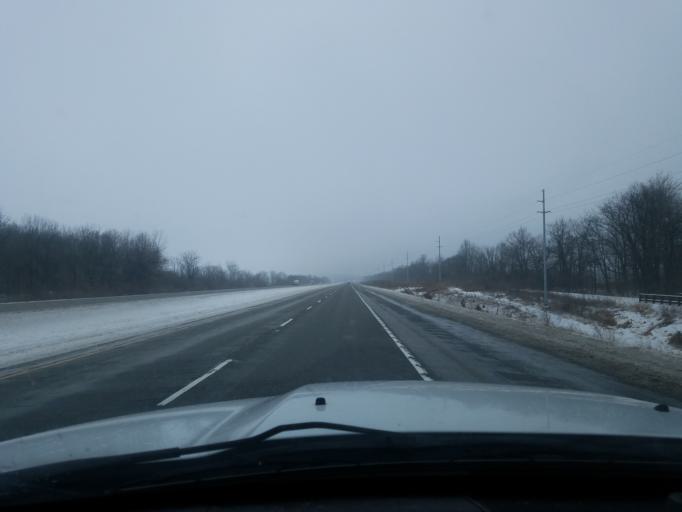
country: US
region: Indiana
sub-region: Fulton County
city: Rochester
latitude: 41.0181
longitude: -86.1733
